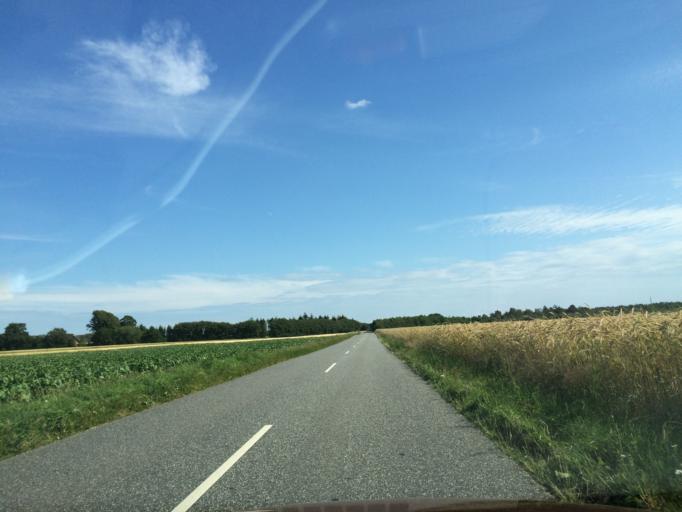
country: DK
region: Central Jutland
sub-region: Syddjurs Kommune
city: Ebeltoft
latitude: 56.2993
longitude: 10.6978
